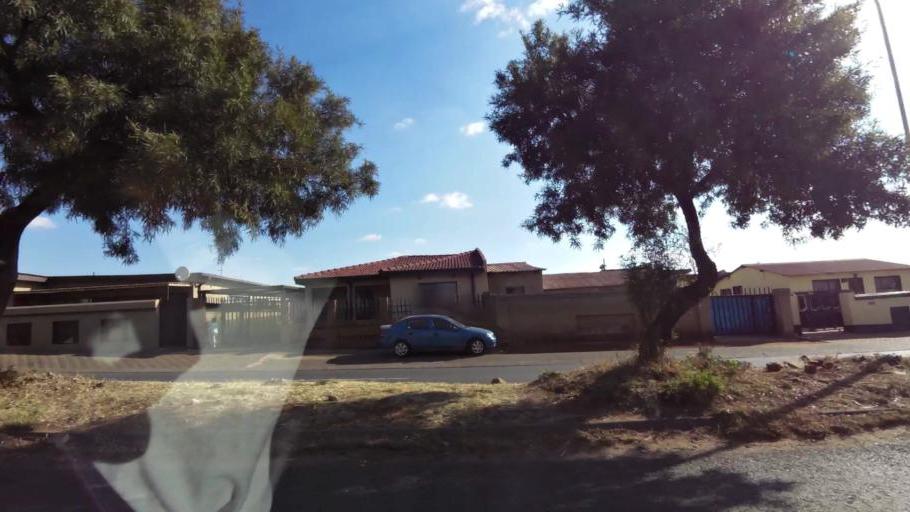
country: ZA
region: Gauteng
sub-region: City of Johannesburg Metropolitan Municipality
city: Soweto
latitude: -26.2235
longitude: 27.8727
